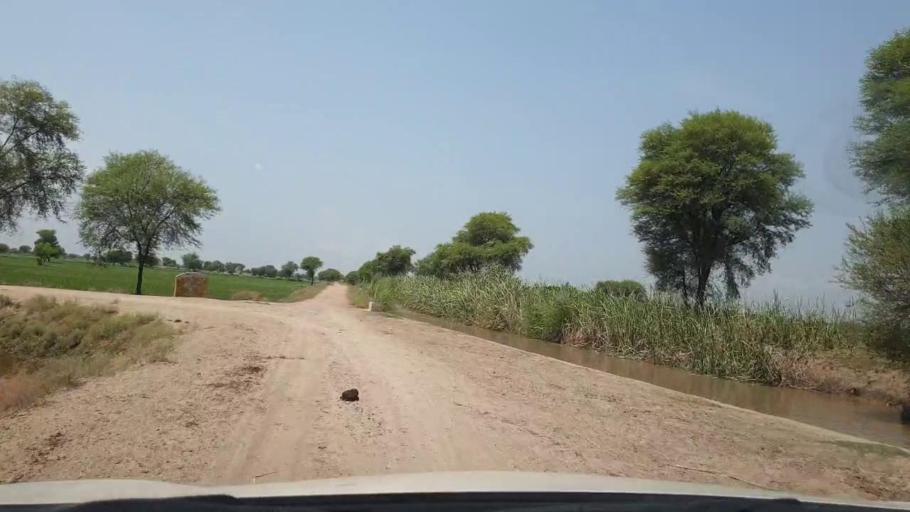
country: PK
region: Sindh
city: Ratodero
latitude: 27.8115
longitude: 68.2432
